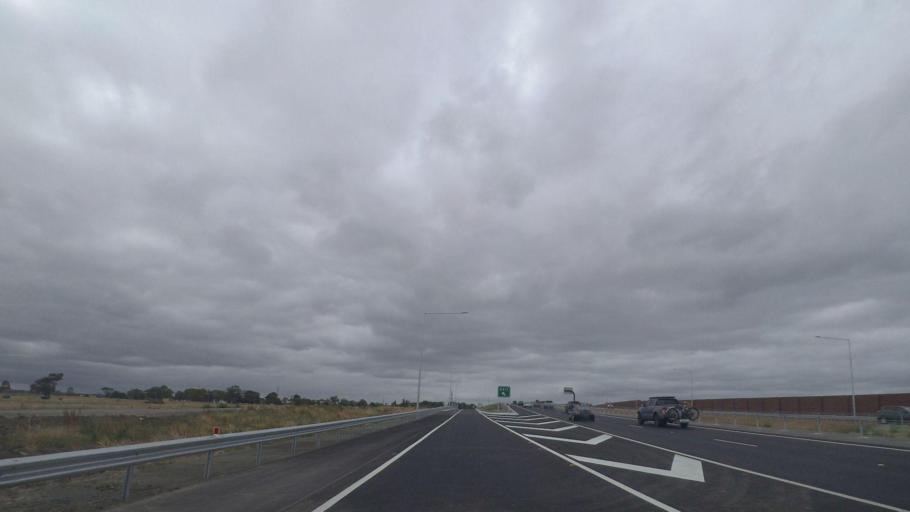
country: AU
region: Victoria
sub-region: Kingston
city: Waterways
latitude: -38.0216
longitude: 145.1298
